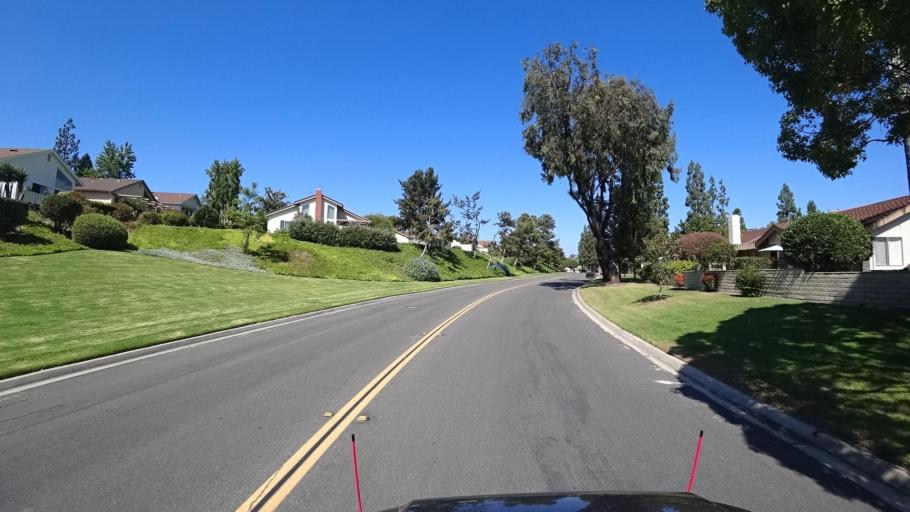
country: US
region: California
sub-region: San Diego County
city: Lake San Marcos
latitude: 33.1223
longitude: -117.2124
